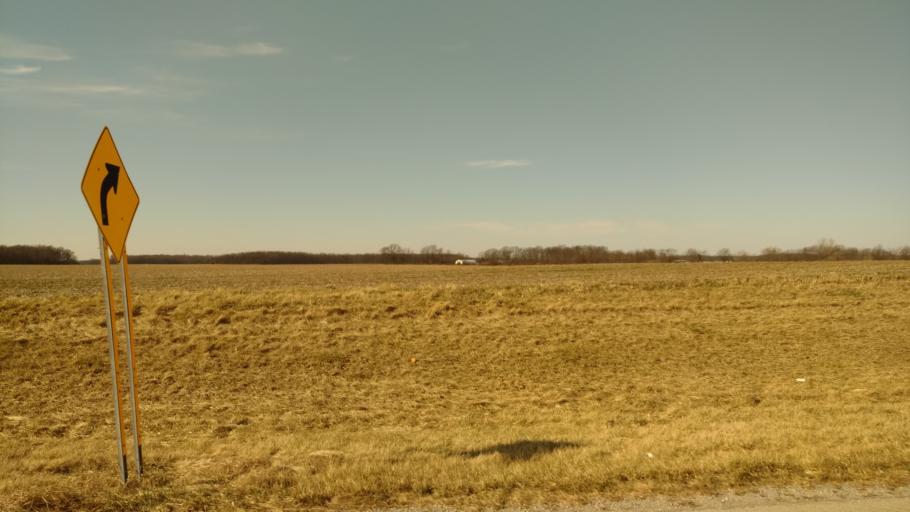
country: US
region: Ohio
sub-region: Hardin County
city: Forest
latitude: 40.6970
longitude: -83.4000
